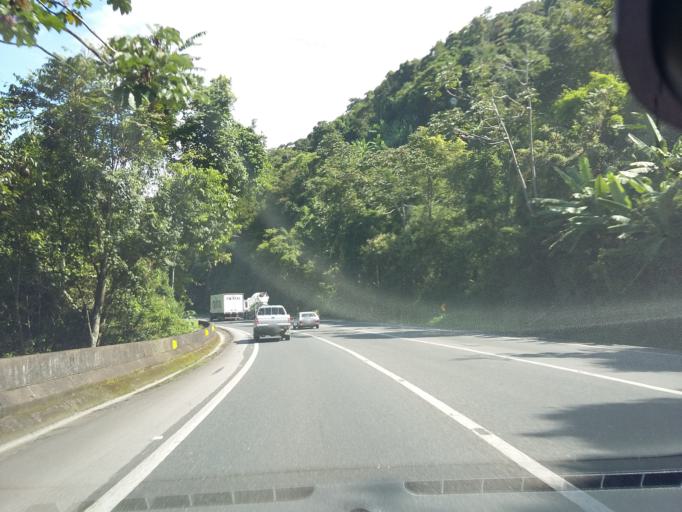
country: BR
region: Santa Catarina
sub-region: Itapema
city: Itapema
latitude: -27.0486
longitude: -48.6005
